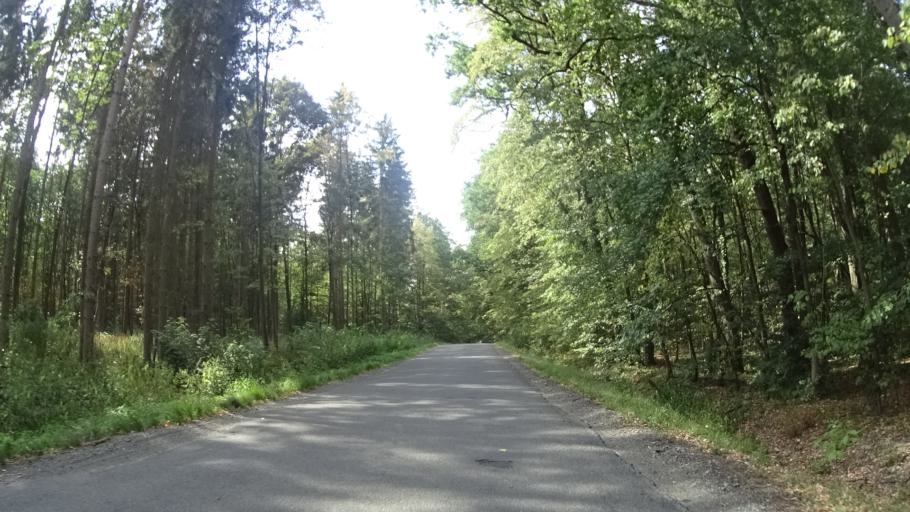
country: CZ
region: Olomoucky
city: Bila Lhota
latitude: 49.7236
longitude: 17.0247
